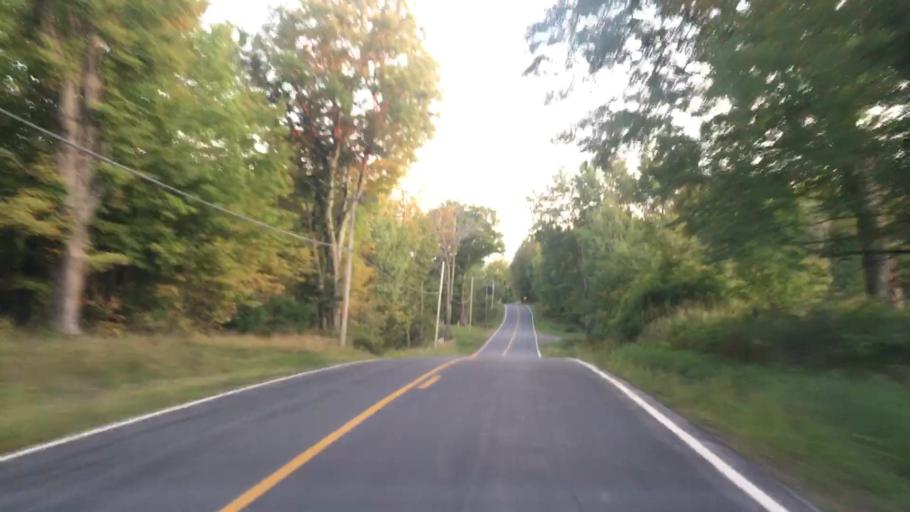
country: US
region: Maine
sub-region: Somerset County
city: Cornville
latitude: 44.8601
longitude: -69.6830
